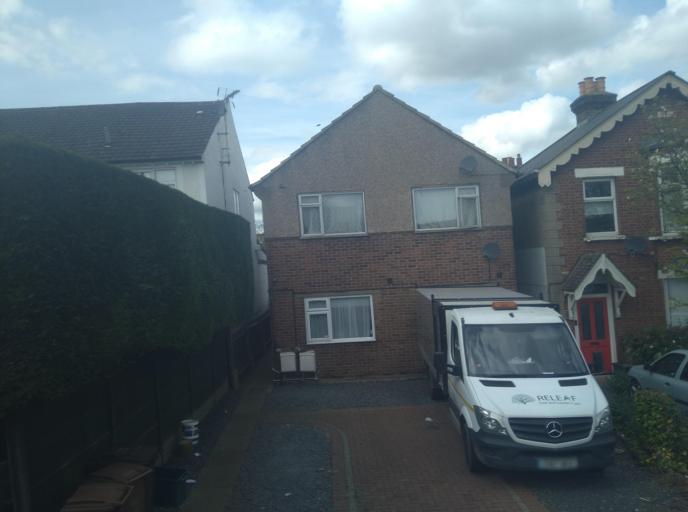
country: GB
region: England
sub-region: Greater London
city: Carshalton
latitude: 51.3656
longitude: -0.1777
